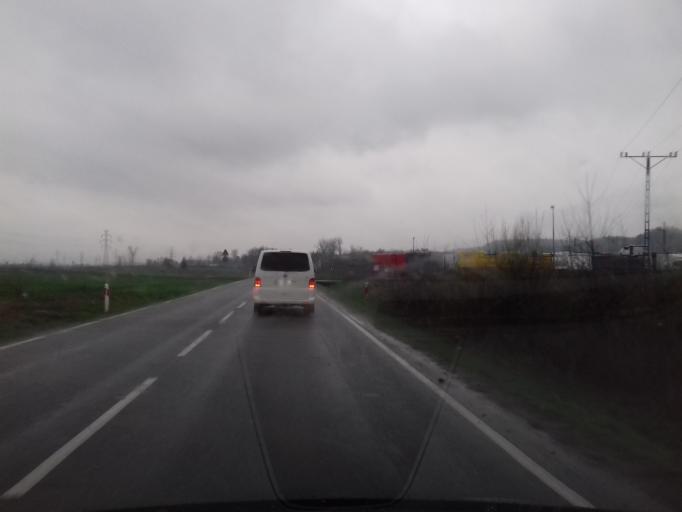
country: PL
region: Lesser Poland Voivodeship
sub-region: Powiat nowosadecki
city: Stary Sacz
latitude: 49.5536
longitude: 20.6548
